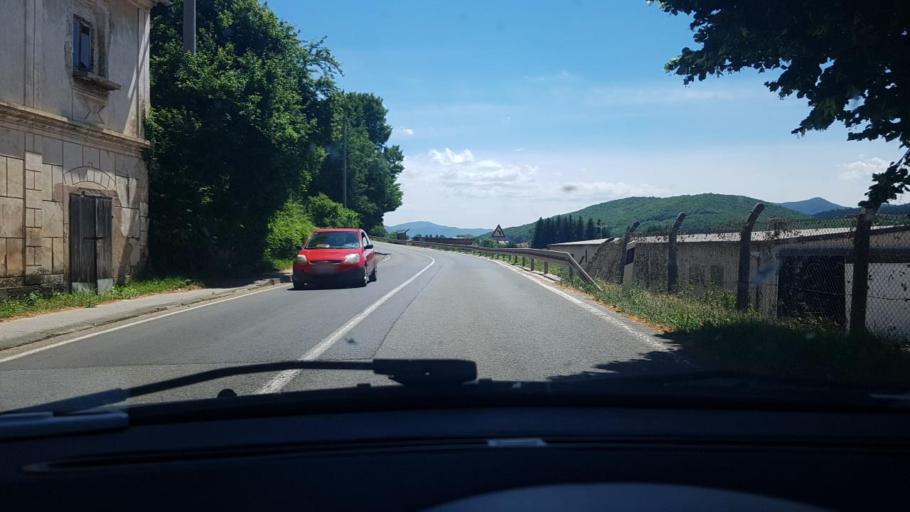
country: HR
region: Licko-Senjska
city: Otocac
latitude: 44.8709
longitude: 15.2219
